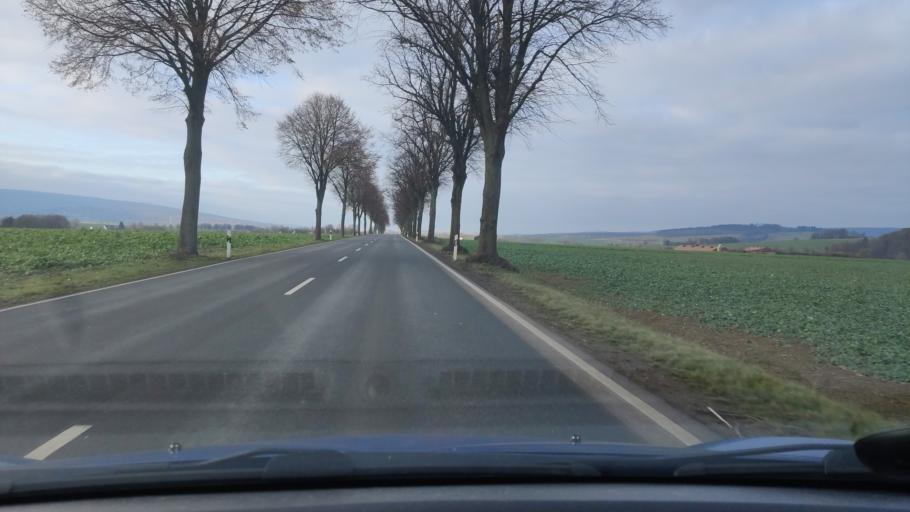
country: DE
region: Lower Saxony
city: Coppenbrugge
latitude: 52.1451
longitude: 9.5106
